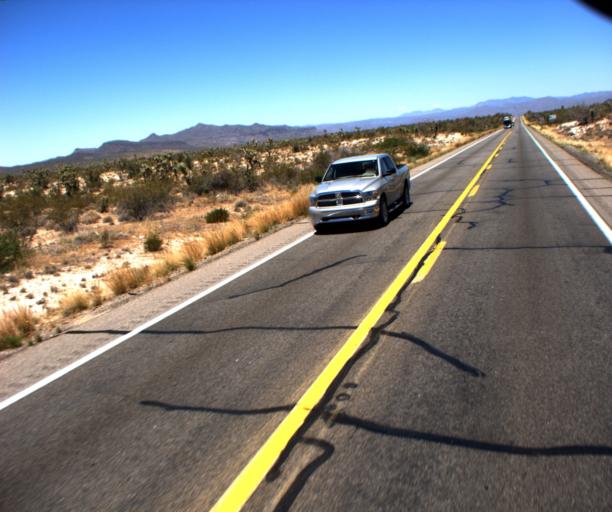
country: US
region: Arizona
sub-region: Yavapai County
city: Congress
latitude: 34.2476
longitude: -113.0803
